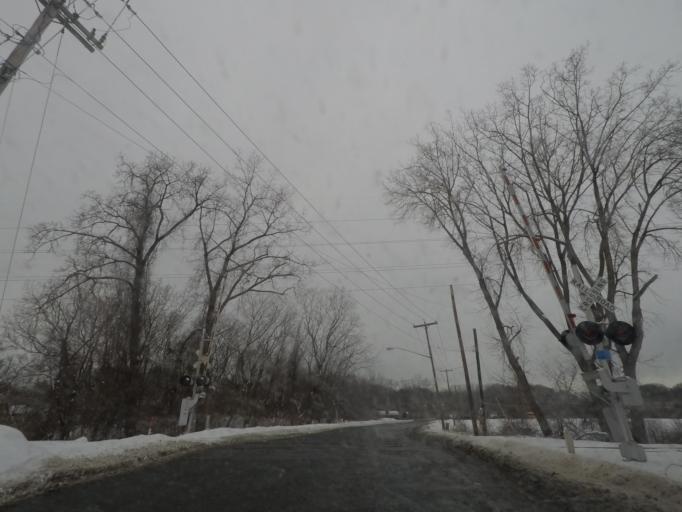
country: US
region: New York
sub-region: Rensselaer County
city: Rensselaer
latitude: 42.6212
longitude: -73.7652
